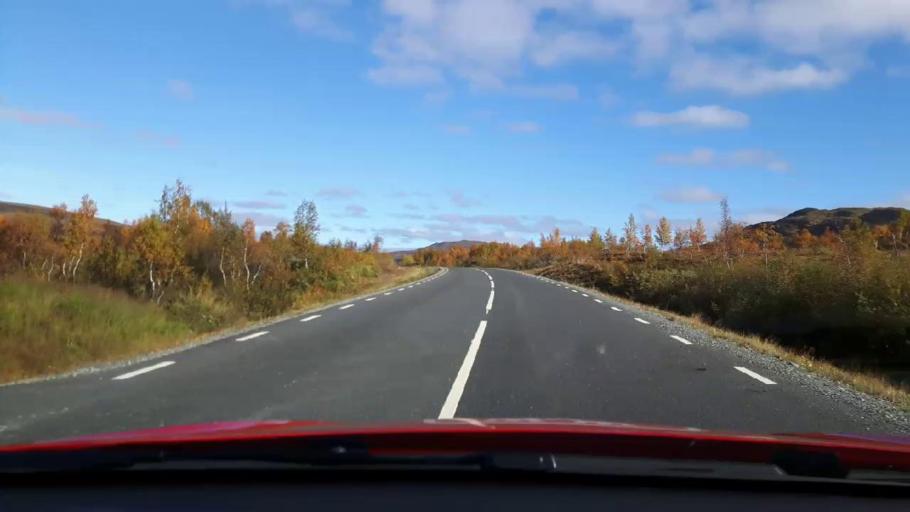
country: NO
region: Nordland
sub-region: Hattfjelldal
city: Hattfjelldal
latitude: 65.0071
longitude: 14.2660
